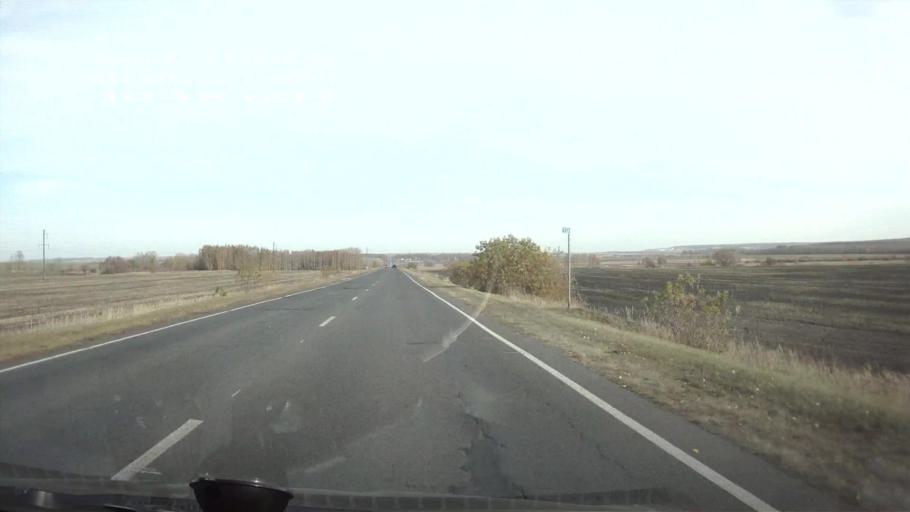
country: RU
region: Mordoviya
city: Atyashevo
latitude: 54.5413
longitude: 45.9363
